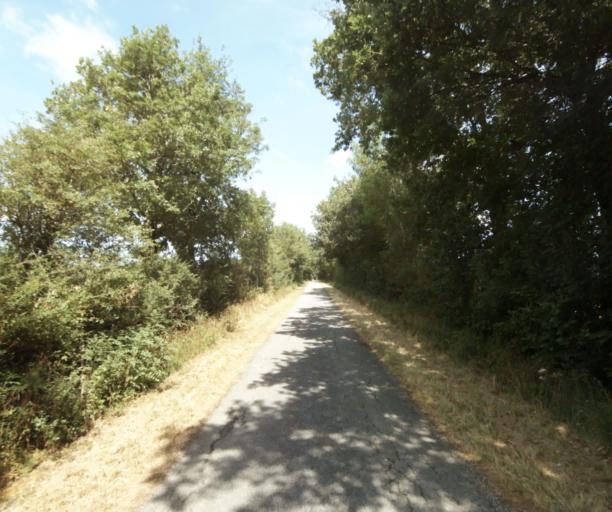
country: FR
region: Midi-Pyrenees
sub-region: Departement du Tarn
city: Dourgne
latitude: 43.4837
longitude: 2.1120
